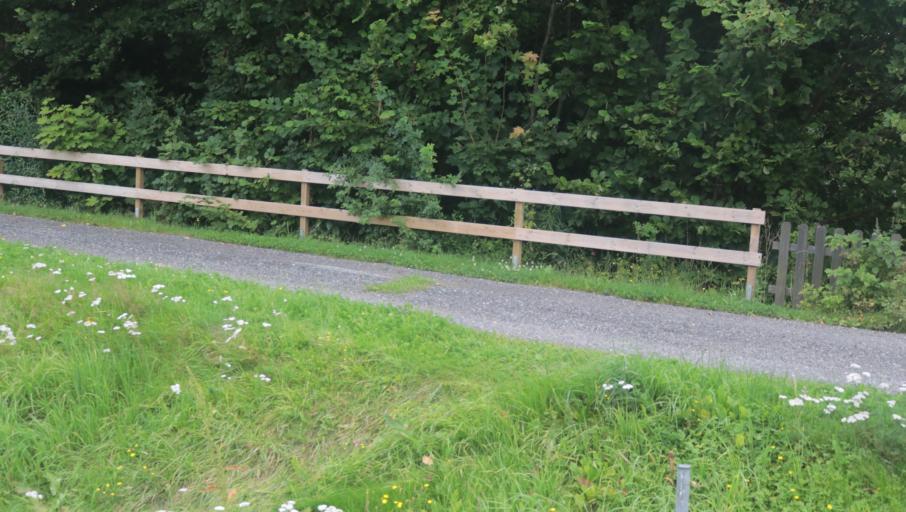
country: SE
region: Blekinge
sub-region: Karlshamns Kommun
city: Karlshamn
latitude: 56.2146
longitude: 14.9524
